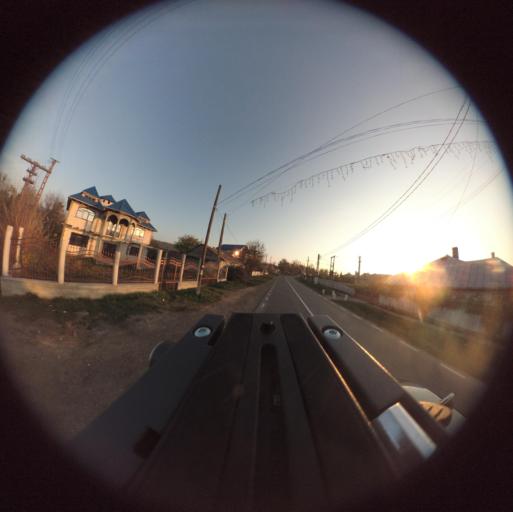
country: RO
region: Vaslui
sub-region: Comuna Bacesti
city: Bacesti
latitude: 46.8269
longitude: 27.2507
